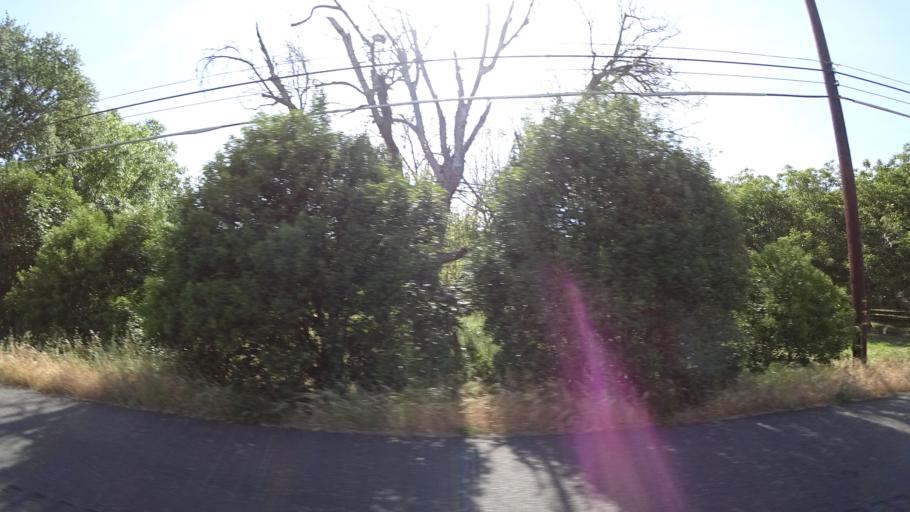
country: US
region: California
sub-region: Tehama County
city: Gerber
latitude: 40.1148
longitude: -122.1176
